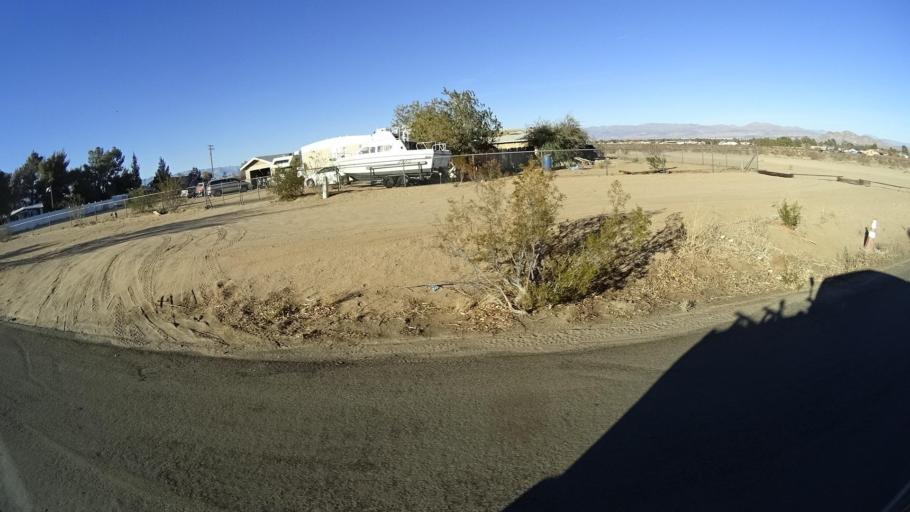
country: US
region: California
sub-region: Kern County
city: Ridgecrest
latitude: 35.6007
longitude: -117.7063
